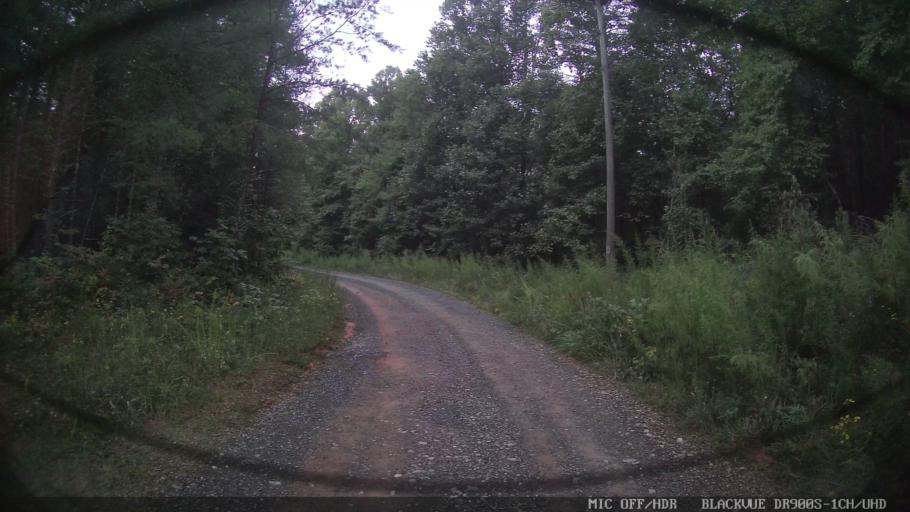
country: US
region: Georgia
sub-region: Gilmer County
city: Ellijay
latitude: 34.7004
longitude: -84.3304
